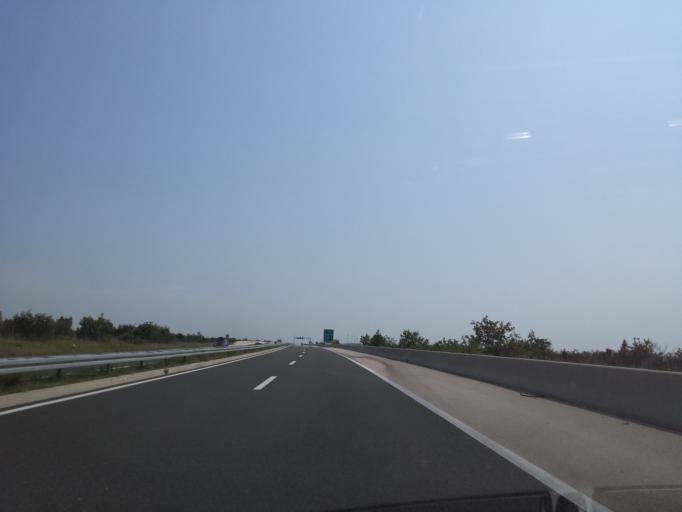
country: HR
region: Zadarska
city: Galovac
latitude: 44.1230
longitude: 15.4314
